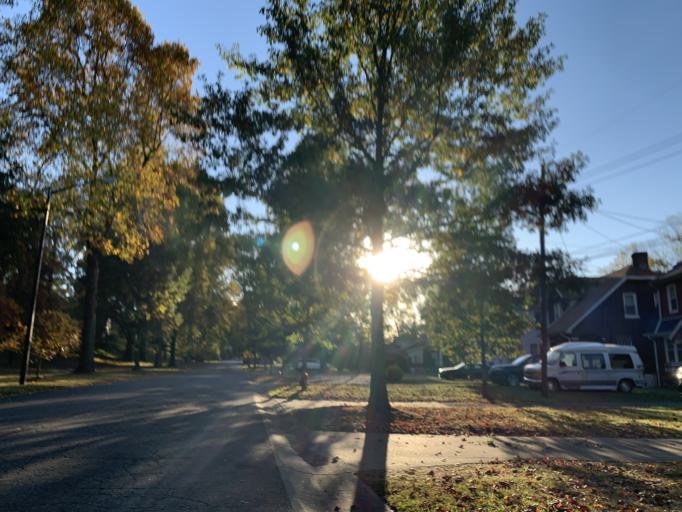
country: US
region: Indiana
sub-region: Floyd County
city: New Albany
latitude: 38.2734
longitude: -85.8157
